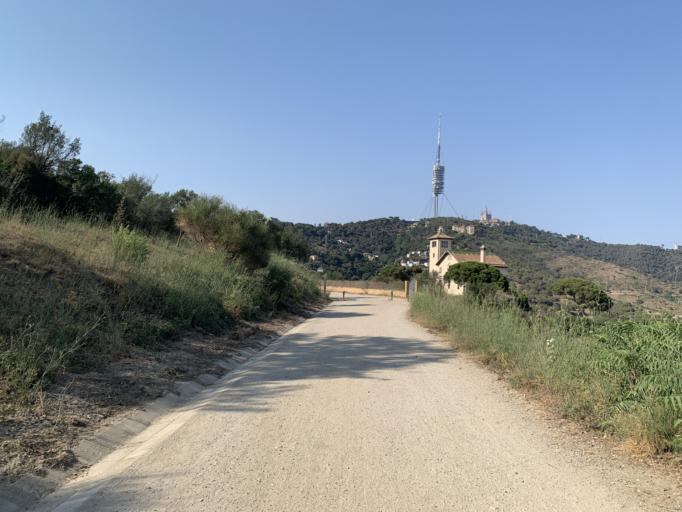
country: ES
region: Catalonia
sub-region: Provincia de Barcelona
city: les Corts
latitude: 41.4062
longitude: 2.1090
